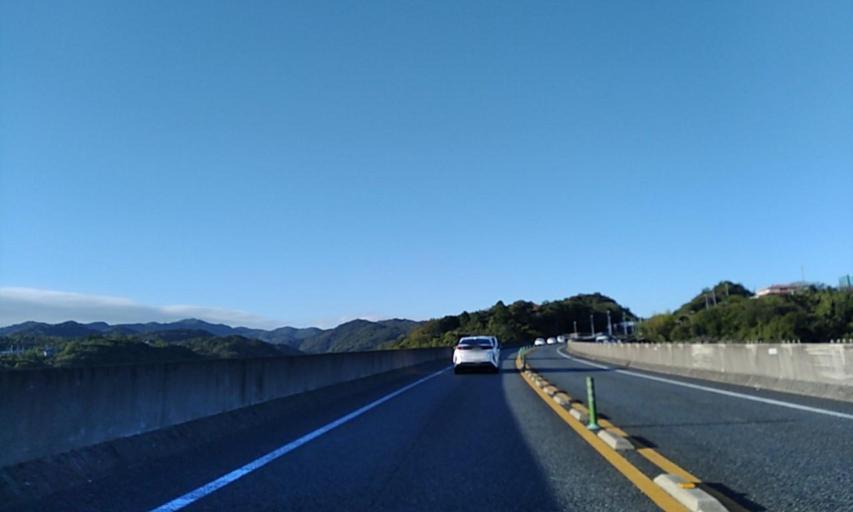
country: JP
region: Wakayama
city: Iwade
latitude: 34.3409
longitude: 135.2485
